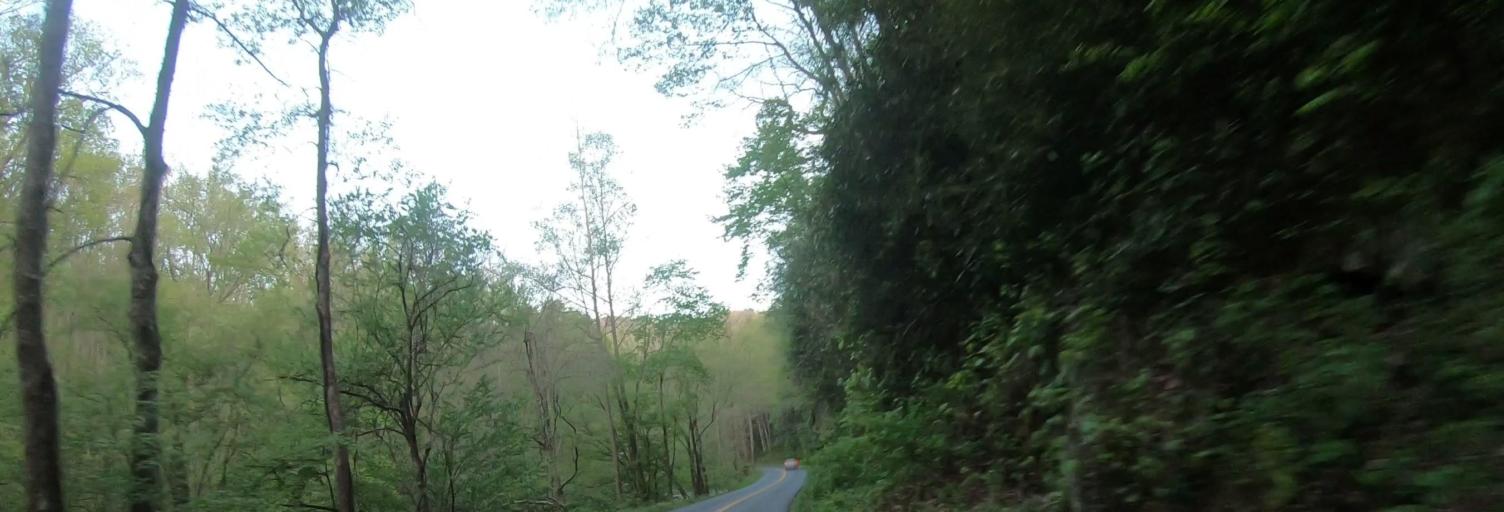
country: US
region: Tennessee
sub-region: Sevier County
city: Gatlinburg
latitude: 35.6691
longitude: -83.6355
